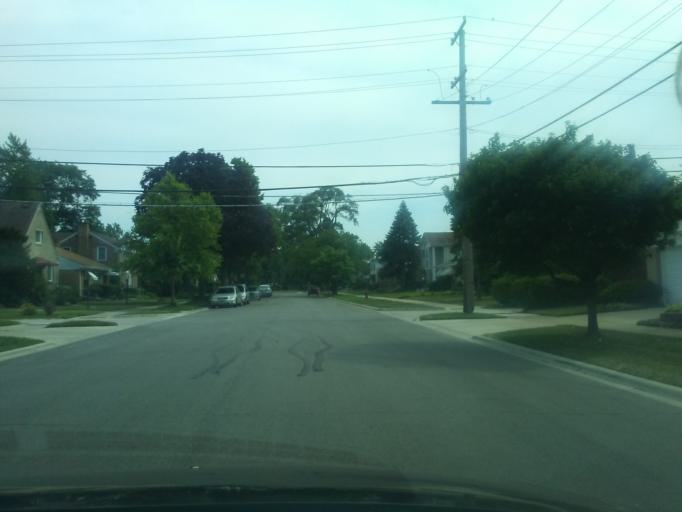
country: US
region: Illinois
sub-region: Cook County
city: Skokie
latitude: 42.0188
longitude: -87.7416
